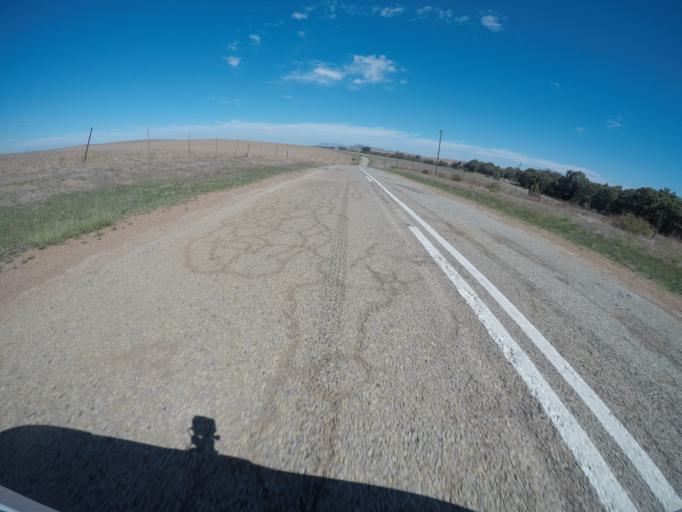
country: ZA
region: Western Cape
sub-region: City of Cape Town
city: Atlantis
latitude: -33.6167
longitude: 18.6344
